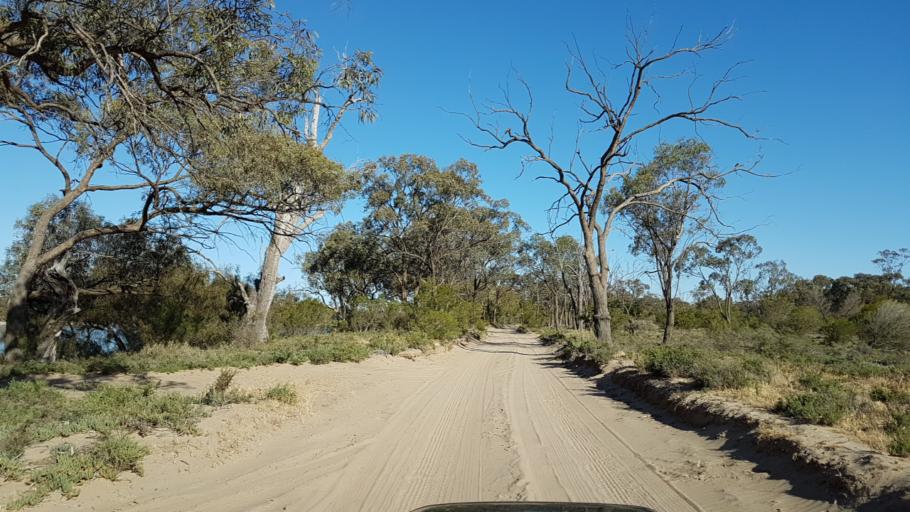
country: AU
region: South Australia
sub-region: Loxton Waikerie
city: Waikerie
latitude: -34.1595
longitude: 140.0290
